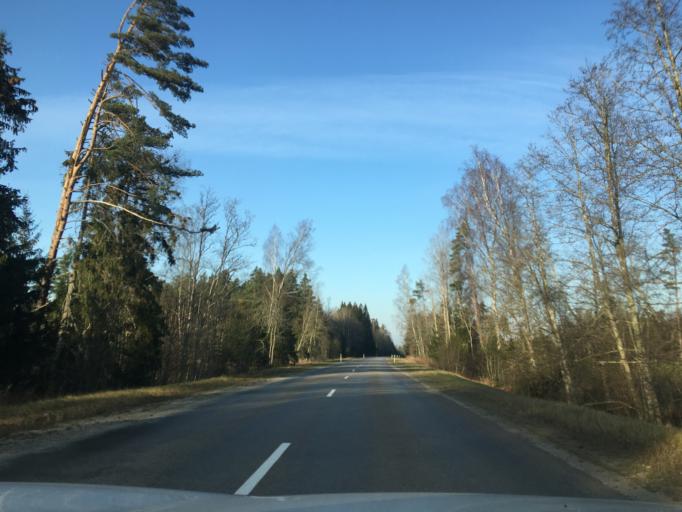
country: LV
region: Kuldigas Rajons
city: Kuldiga
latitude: 57.0447
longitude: 21.8260
